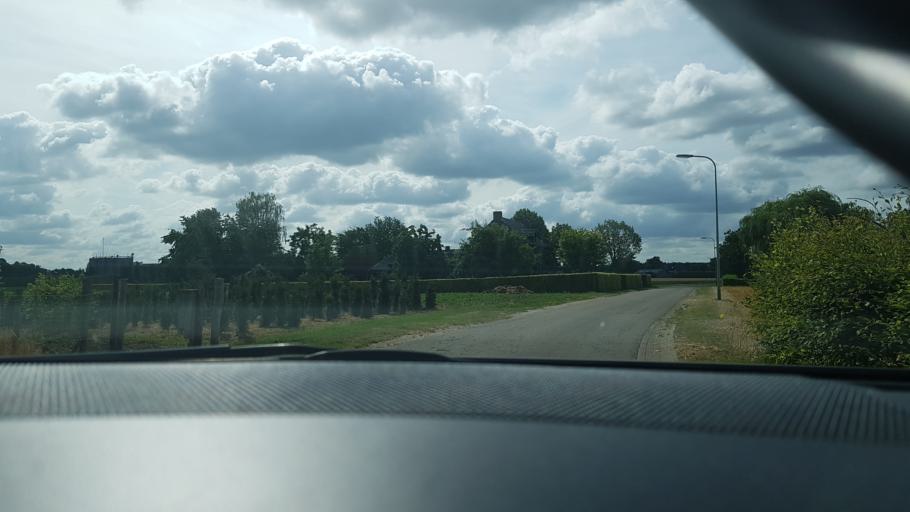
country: NL
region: Limburg
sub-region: Gemeente Beesel
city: Beesel
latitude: 51.2392
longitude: 6.0242
